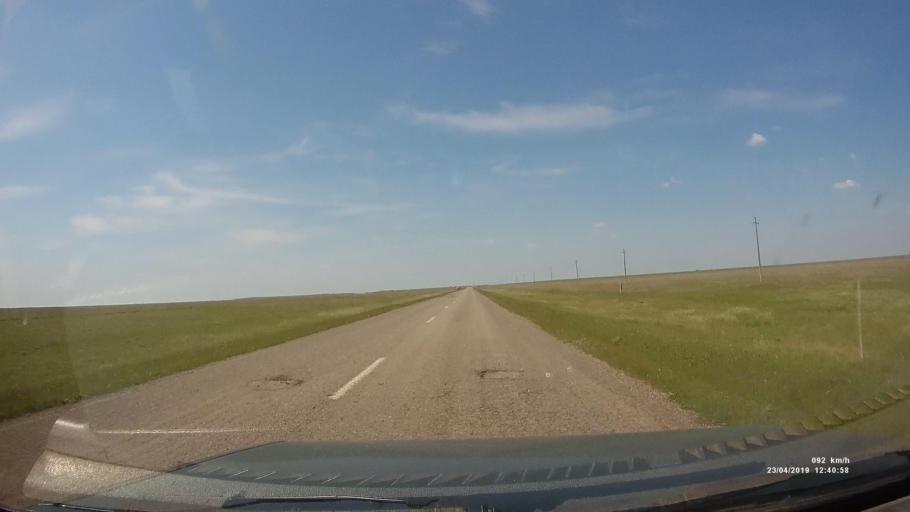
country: RU
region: Kalmykiya
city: Yashalta
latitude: 46.4446
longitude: 42.6882
